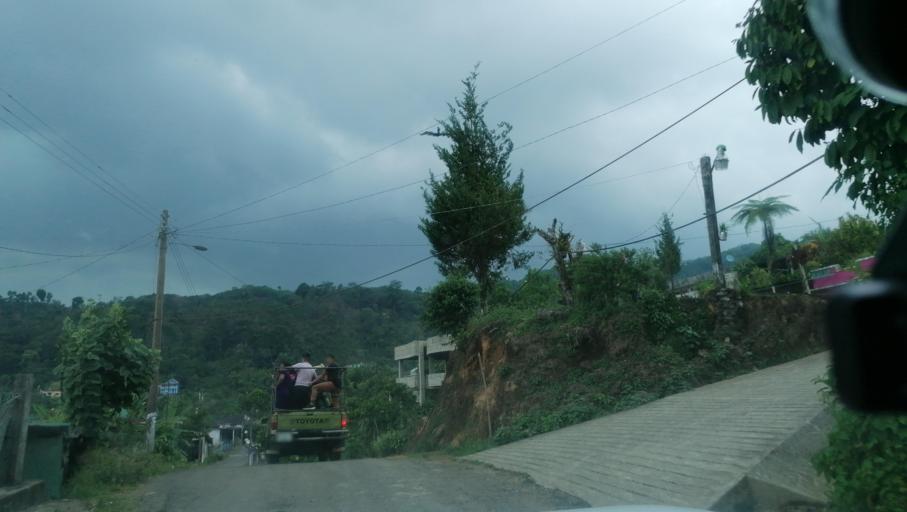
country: MX
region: Chiapas
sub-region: Cacahoatan
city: Benito Juarez
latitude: 15.0733
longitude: -92.1691
